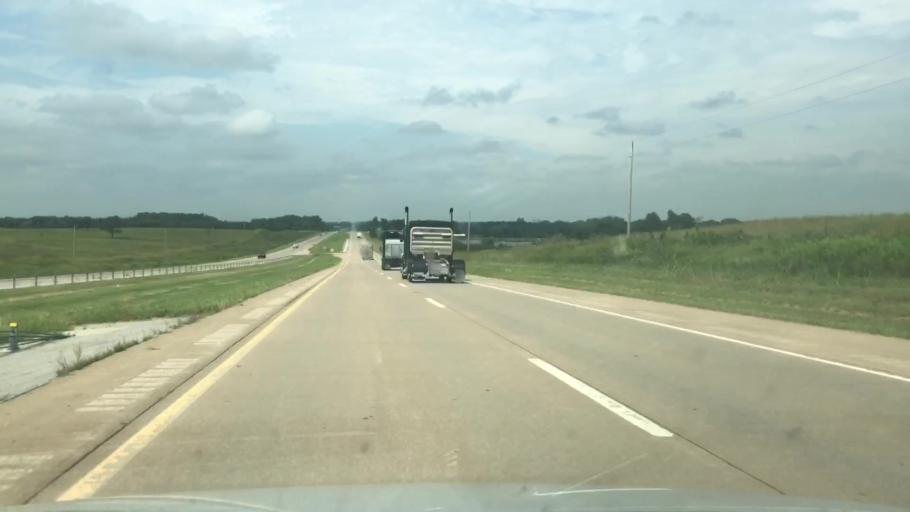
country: US
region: Oklahoma
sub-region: Washington County
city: Bartlesville
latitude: 36.6301
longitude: -95.9354
